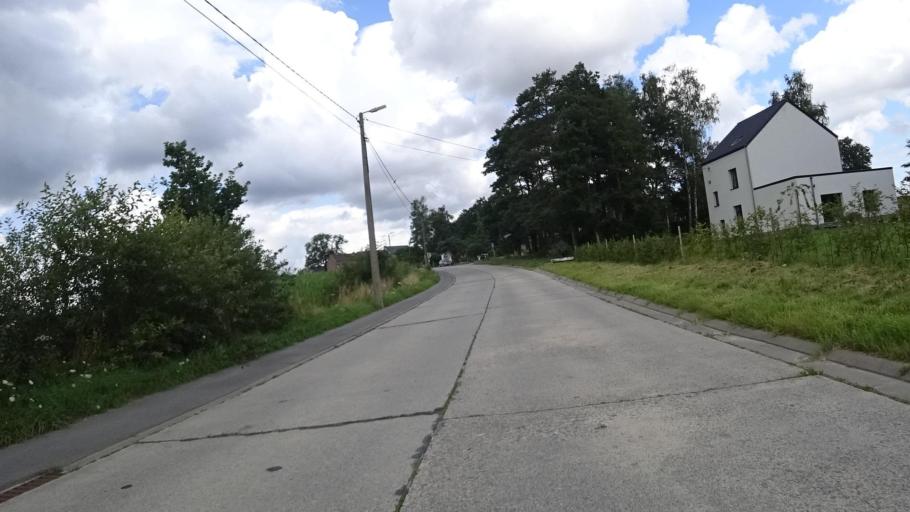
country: BE
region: Wallonia
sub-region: Province du Brabant Wallon
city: Villers-la-Ville
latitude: 50.5663
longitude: 4.5626
